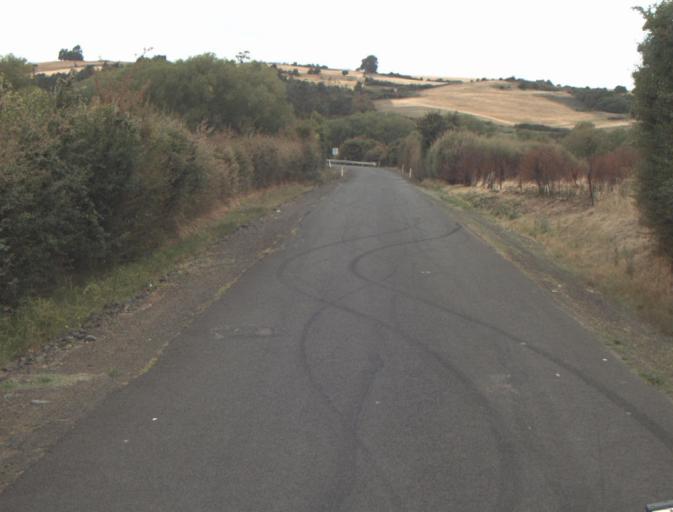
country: AU
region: Tasmania
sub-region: Northern Midlands
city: Evandale
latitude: -41.5316
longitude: 147.2422
